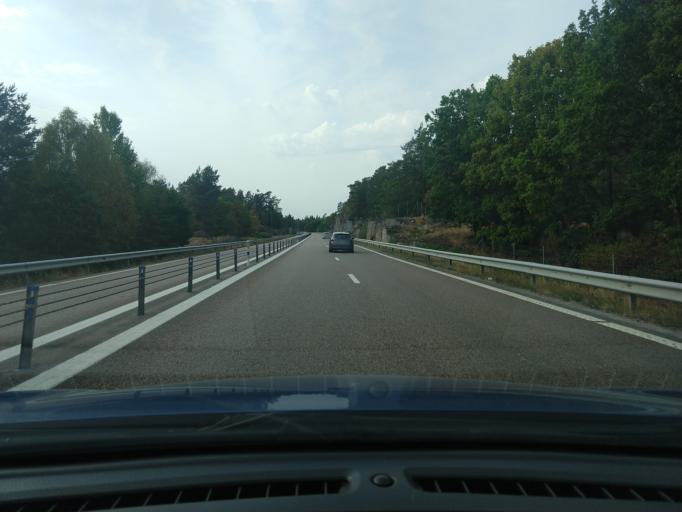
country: SE
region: Blekinge
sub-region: Ronneby Kommun
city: Kallinge
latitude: 56.2086
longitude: 15.3242
